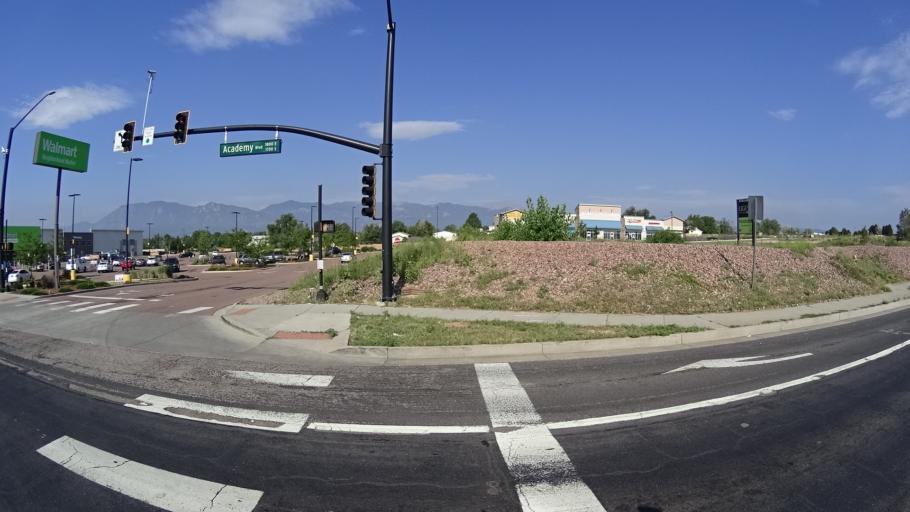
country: US
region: Colorado
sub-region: El Paso County
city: Stratmoor
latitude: 38.8086
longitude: -104.7576
